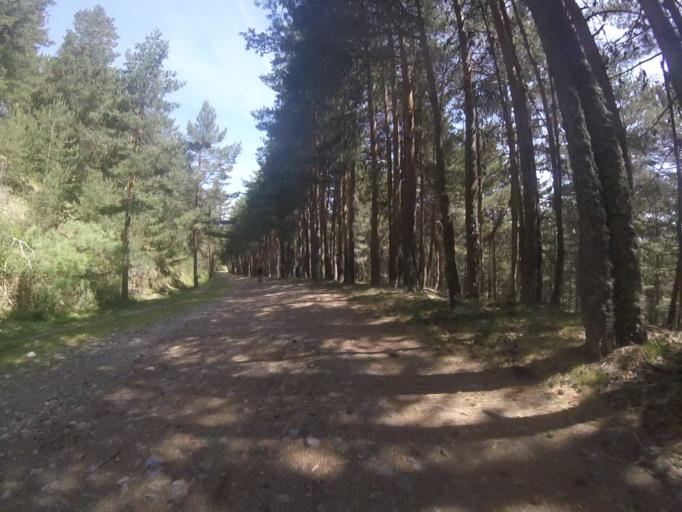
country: ES
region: Madrid
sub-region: Provincia de Madrid
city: Cercedilla
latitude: 40.8106
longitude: -4.0564
